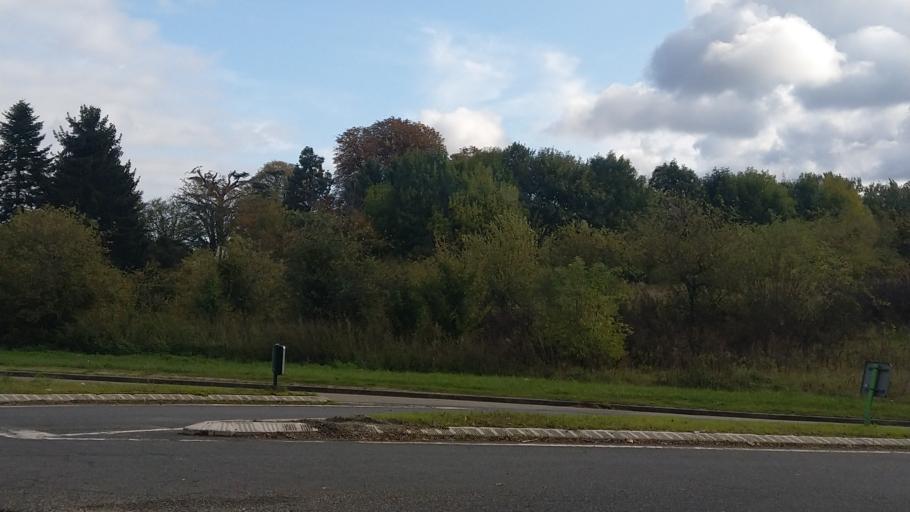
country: FR
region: Ile-de-France
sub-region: Departement du Val-d'Oise
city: Baillet-en-France
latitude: 49.0577
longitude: 2.2893
